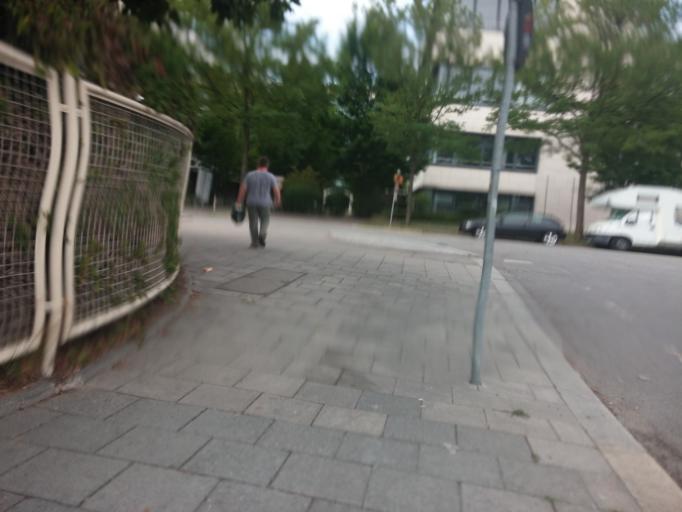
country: DE
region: Bavaria
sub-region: Upper Bavaria
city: Bogenhausen
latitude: 48.1319
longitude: 11.6241
